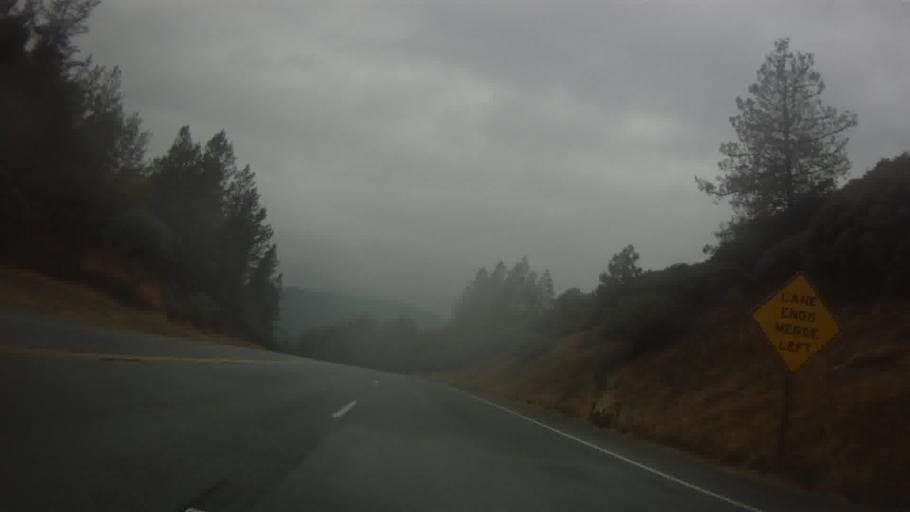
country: US
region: California
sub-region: Shasta County
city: Shasta
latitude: 40.5912
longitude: -122.4706
